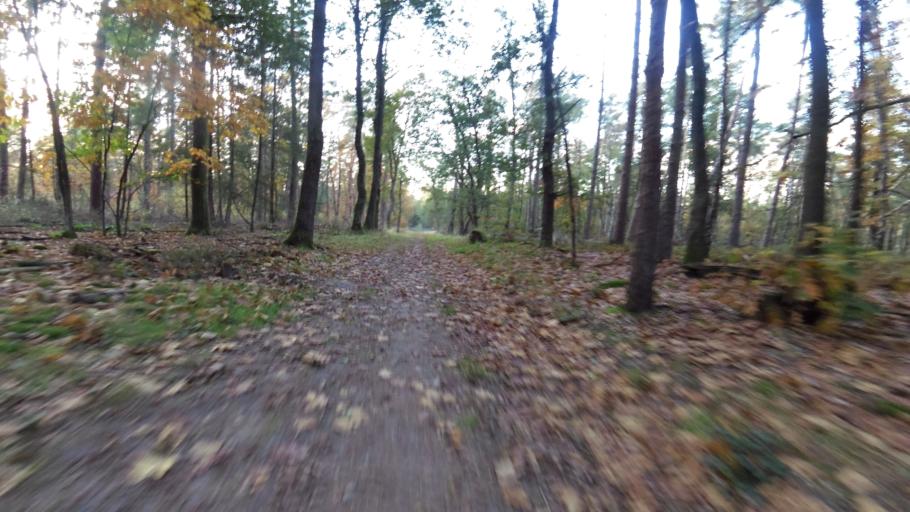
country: NL
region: Gelderland
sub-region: Gemeente Epe
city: Epe
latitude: 52.3669
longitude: 5.9679
